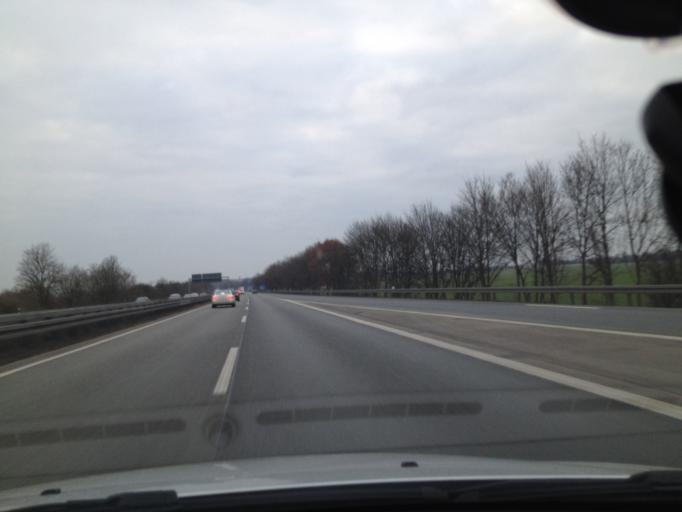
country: DE
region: Hesse
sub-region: Regierungsbezirk Giessen
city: Hoernsheim
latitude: 50.5248
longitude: 8.6338
